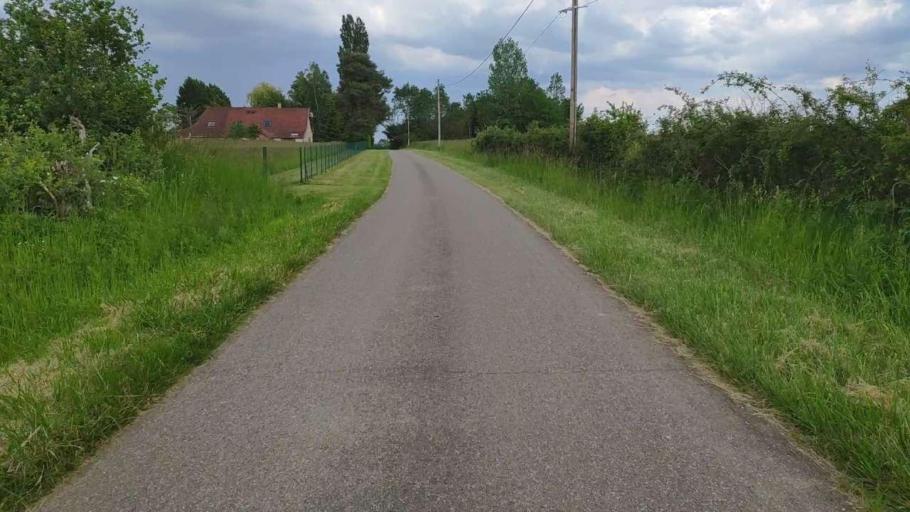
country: FR
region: Franche-Comte
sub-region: Departement du Jura
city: Bletterans
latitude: 46.7940
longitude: 5.3582
